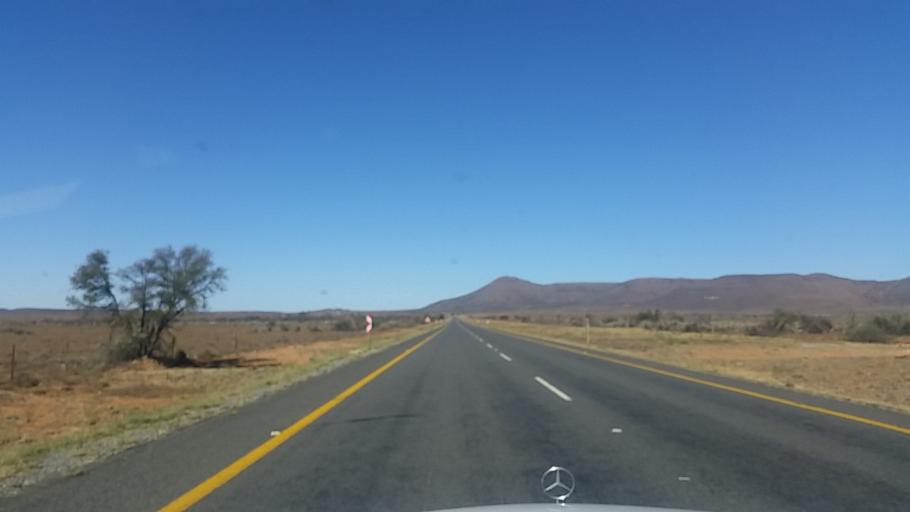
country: ZA
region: Eastern Cape
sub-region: Cacadu District Municipality
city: Graaff-Reinet
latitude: -32.0092
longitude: 24.6546
